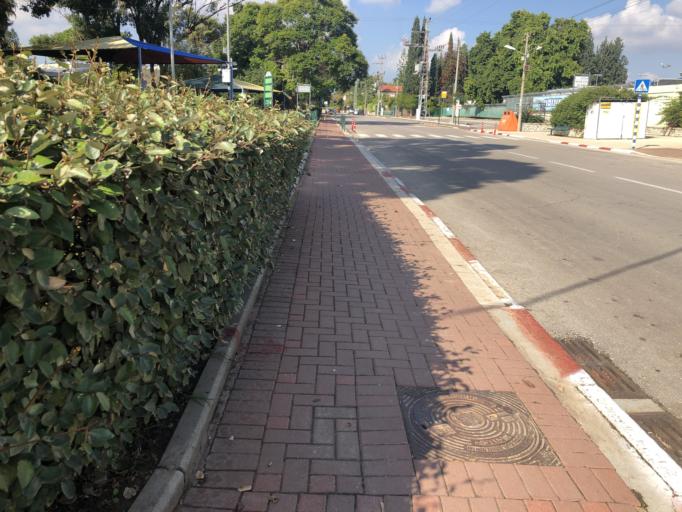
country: IL
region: Central District
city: Yehud
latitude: 32.0304
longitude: 34.8746
